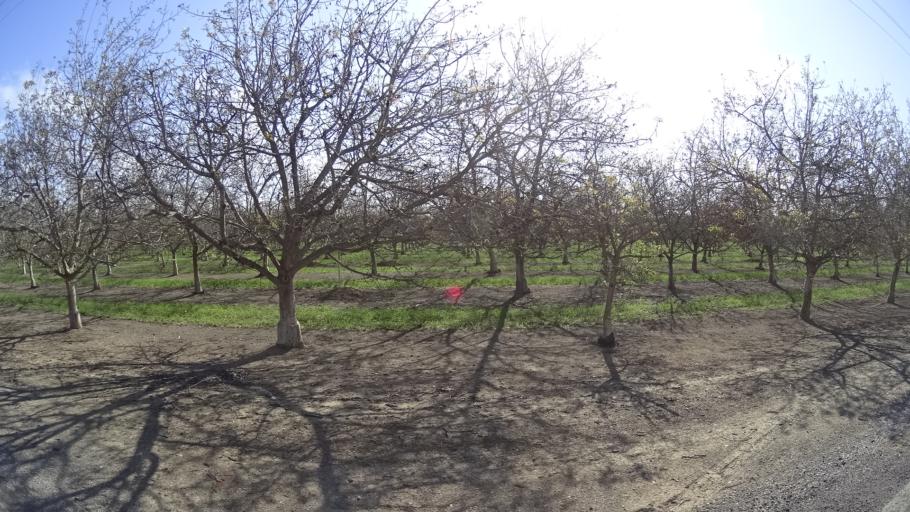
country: US
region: California
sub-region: Glenn County
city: Willows
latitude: 39.4679
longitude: -121.9678
